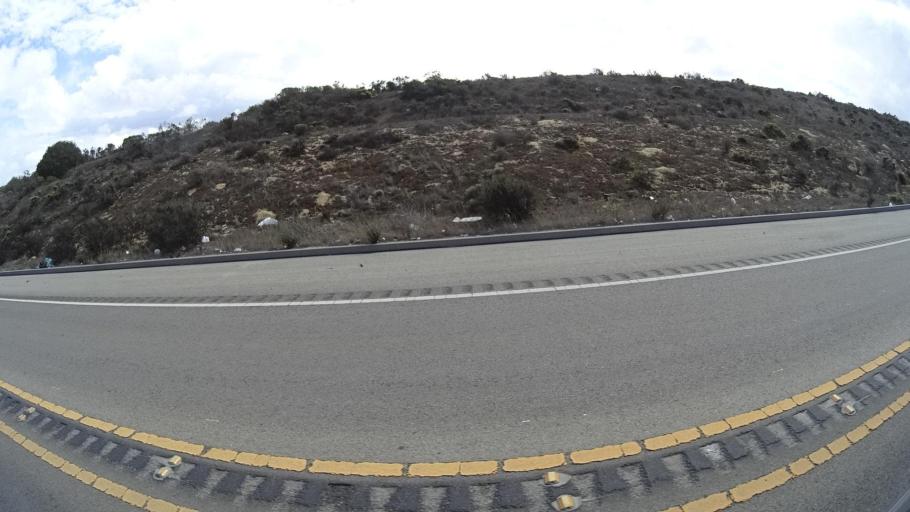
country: US
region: California
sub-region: Monterey County
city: Marina
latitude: 36.6725
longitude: -121.7574
